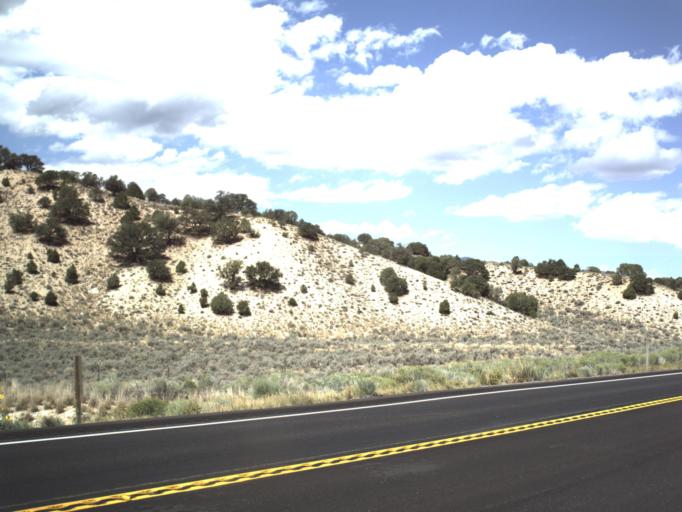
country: US
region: Utah
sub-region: Sevier County
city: Aurora
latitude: 38.9835
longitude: -111.9935
